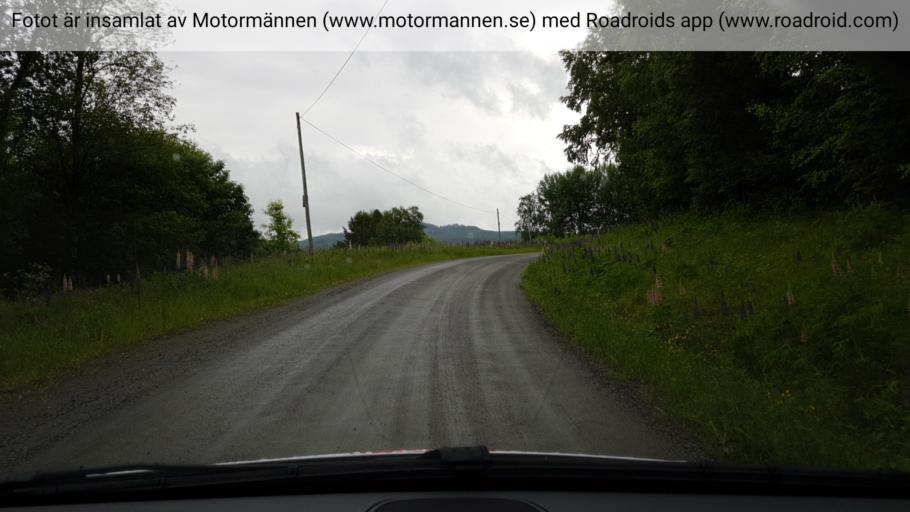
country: SE
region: Jaemtland
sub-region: Stroemsunds Kommun
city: Stroemsund
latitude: 64.2844
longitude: 15.0170
